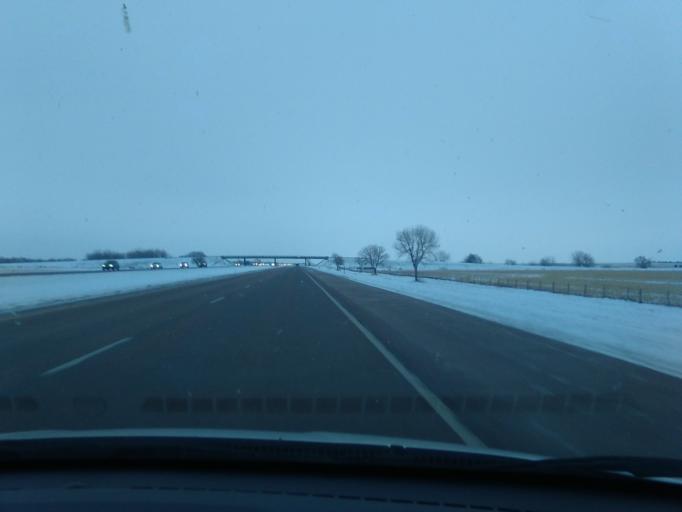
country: US
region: Nebraska
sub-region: Keith County
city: Ogallala
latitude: 41.1204
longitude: -101.6588
